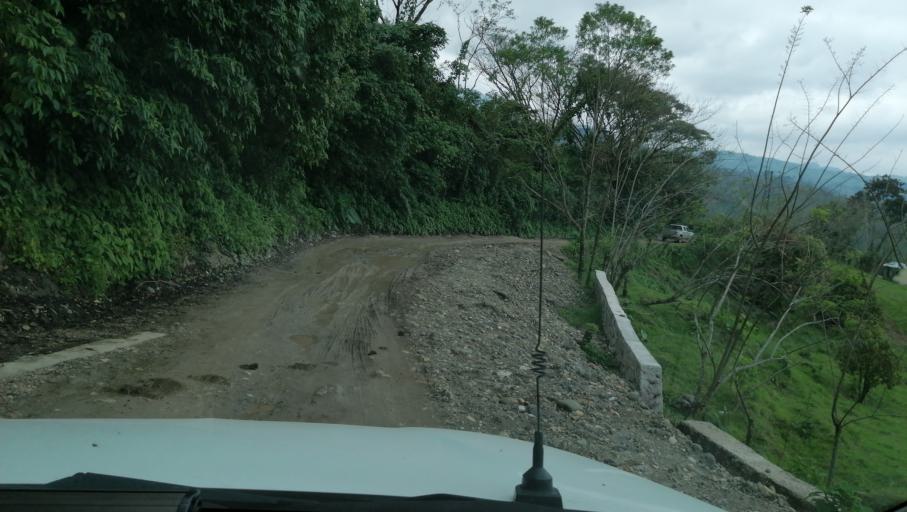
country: MX
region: Chiapas
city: Ocotepec
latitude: 17.2812
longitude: -93.2251
